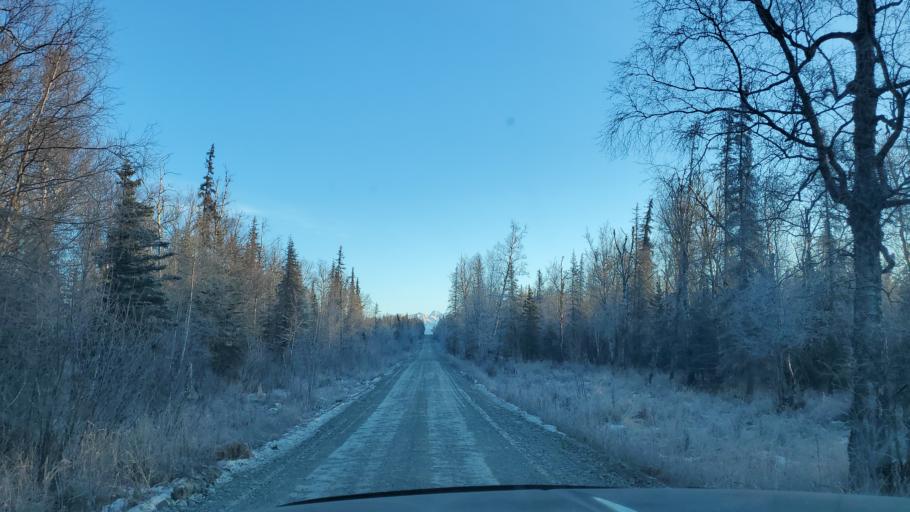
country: US
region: Alaska
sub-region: Matanuska-Susitna Borough
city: Lakes
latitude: 61.6428
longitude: -149.3566
